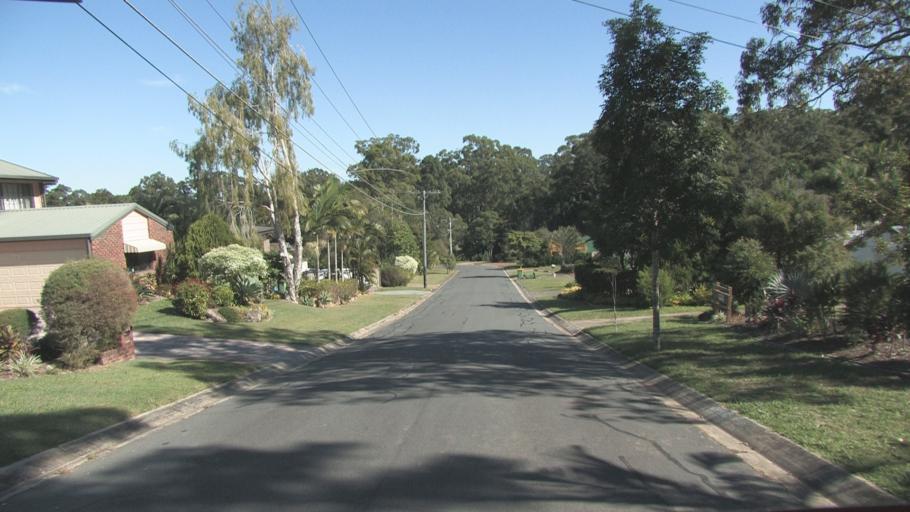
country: AU
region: Queensland
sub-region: Logan
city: Slacks Creek
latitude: -27.6379
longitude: 153.1629
